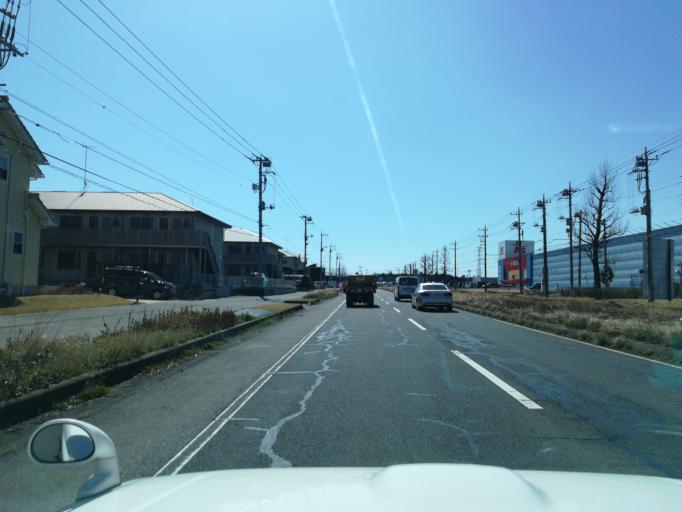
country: JP
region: Ibaraki
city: Naka
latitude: 36.0131
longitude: 140.1462
